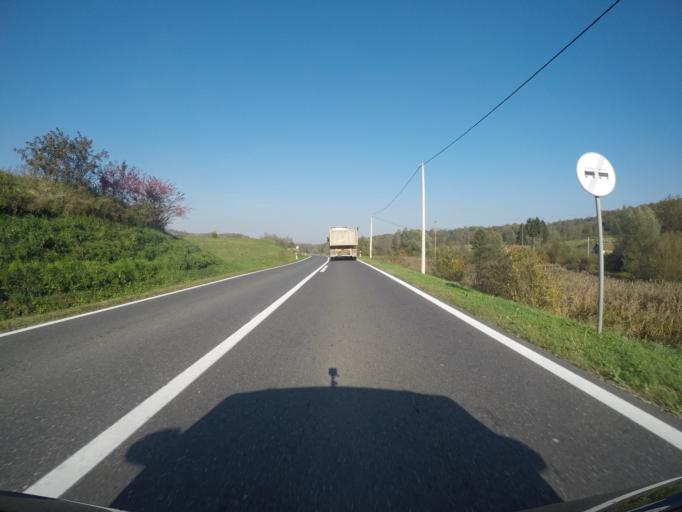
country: HR
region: Koprivnicko-Krizevacka
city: Virje
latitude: 45.9973
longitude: 16.9167
